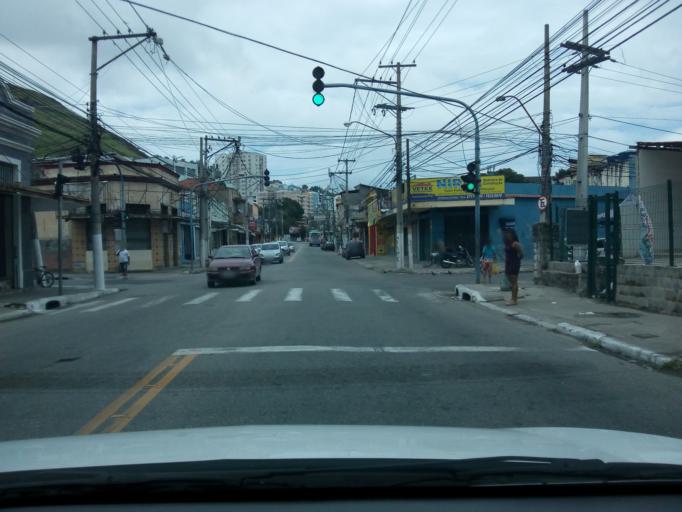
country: BR
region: Rio de Janeiro
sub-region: Niteroi
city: Niteroi
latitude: -22.8699
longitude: -43.1045
